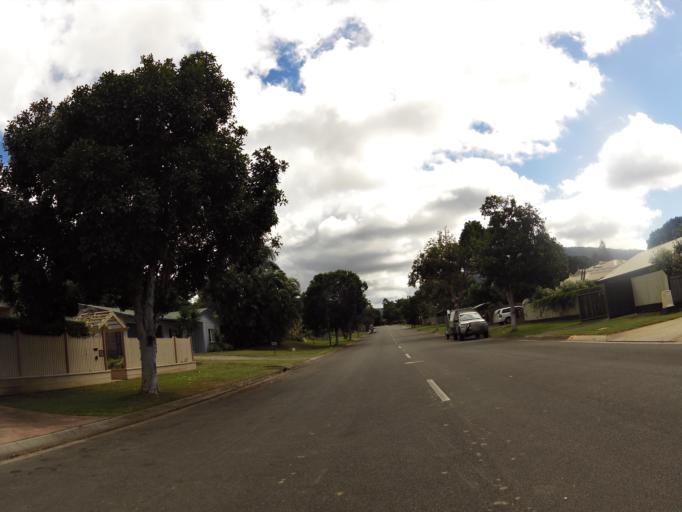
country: AU
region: Queensland
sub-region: Cairns
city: Redlynch
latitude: -16.8818
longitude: 145.6938
